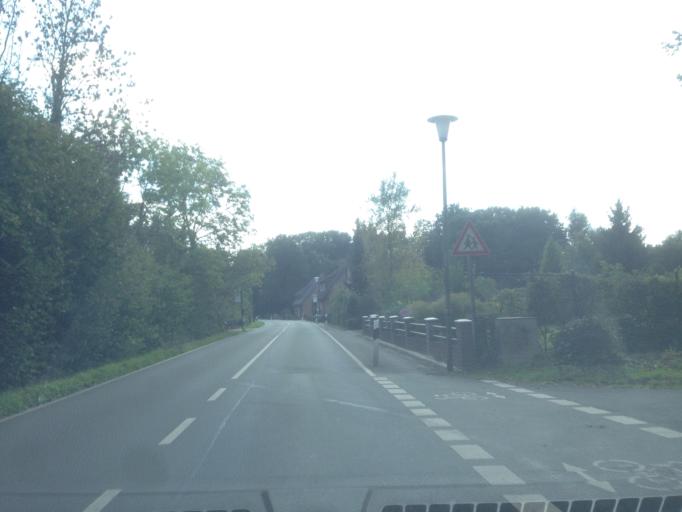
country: DE
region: North Rhine-Westphalia
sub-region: Regierungsbezirk Munster
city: Muenster
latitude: 52.0173
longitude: 7.6034
